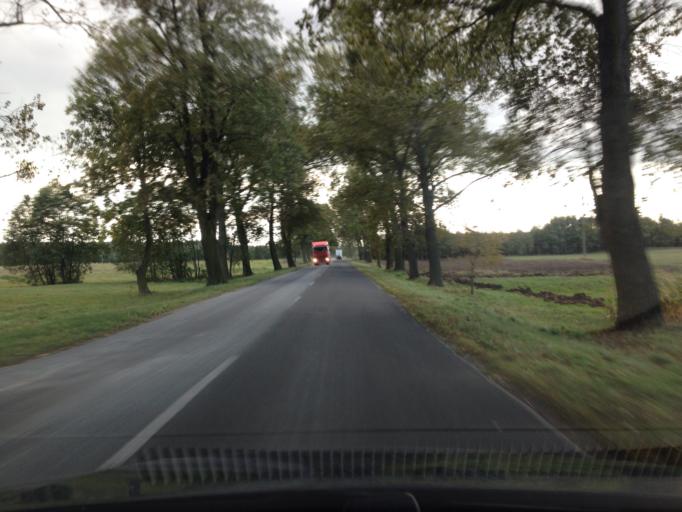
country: PL
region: Kujawsko-Pomorskie
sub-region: Powiat lipnowski
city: Chrostkowo
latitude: 52.9630
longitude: 19.3148
